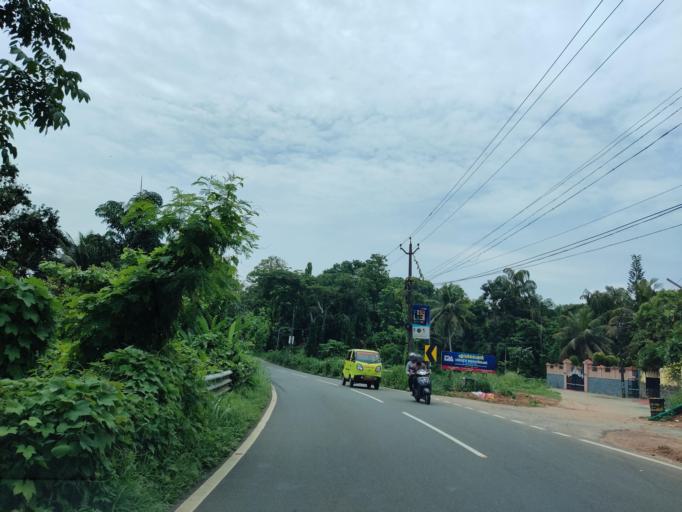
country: IN
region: Kerala
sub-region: Alappuzha
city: Chengannur
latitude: 9.2989
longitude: 76.6271
